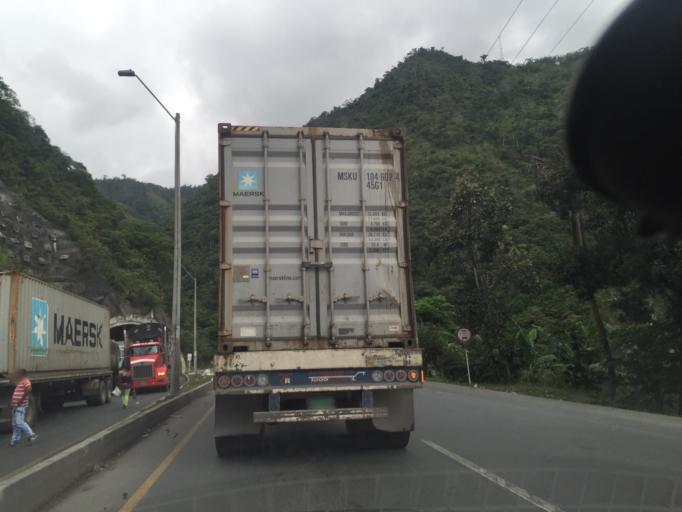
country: CO
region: Valle del Cauca
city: Dagua
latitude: 3.7747
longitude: -76.7442
